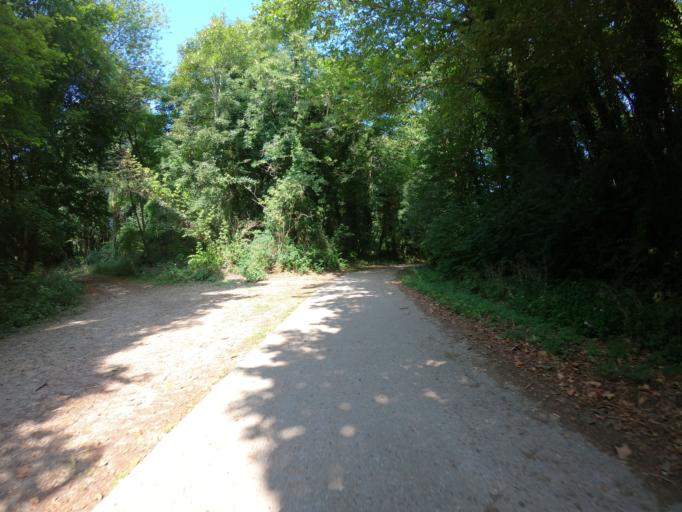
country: FR
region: Ile-de-France
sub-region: Departement de l'Essonne
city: Bievres
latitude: 48.7665
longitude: 2.2374
